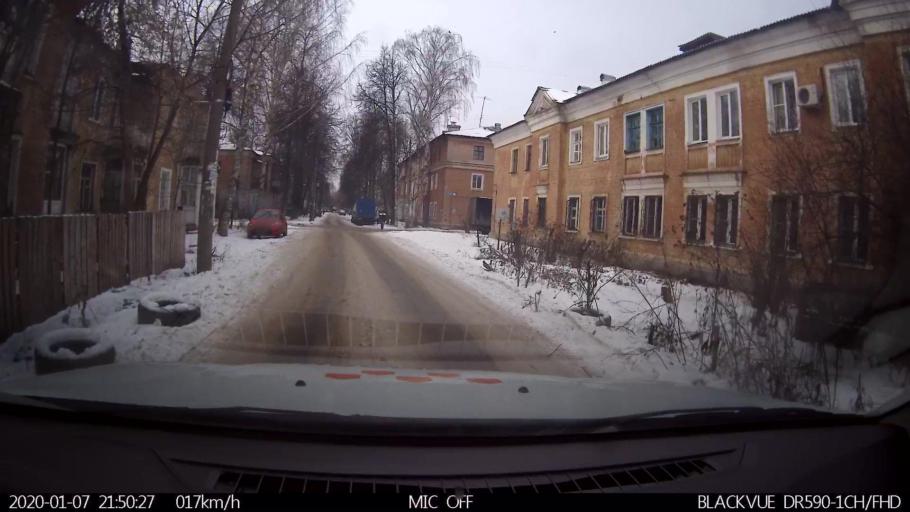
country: RU
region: Nizjnij Novgorod
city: Nizhniy Novgorod
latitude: 56.3164
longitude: 43.8895
